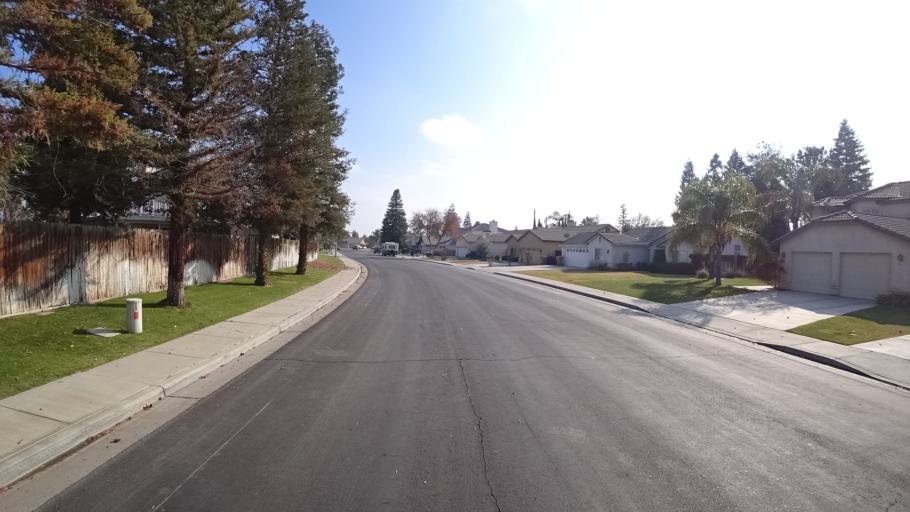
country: US
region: California
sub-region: Kern County
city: Greenacres
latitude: 35.3014
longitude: -119.0855
